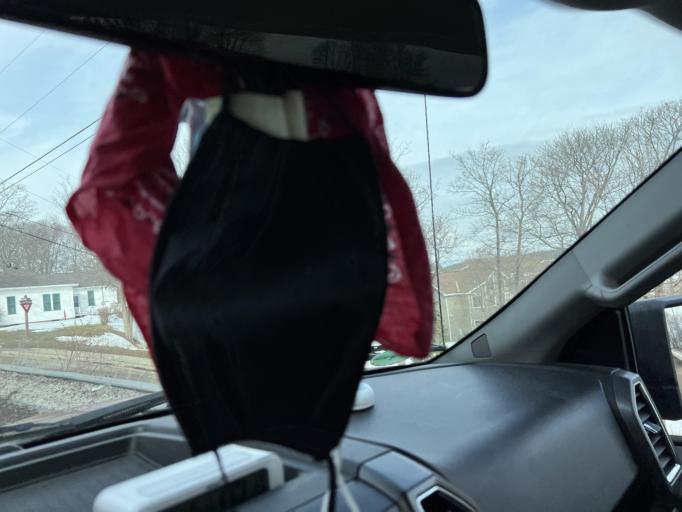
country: US
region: Michigan
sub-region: Mackinac County
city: Saint Ignace
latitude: 45.8674
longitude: -84.7278
